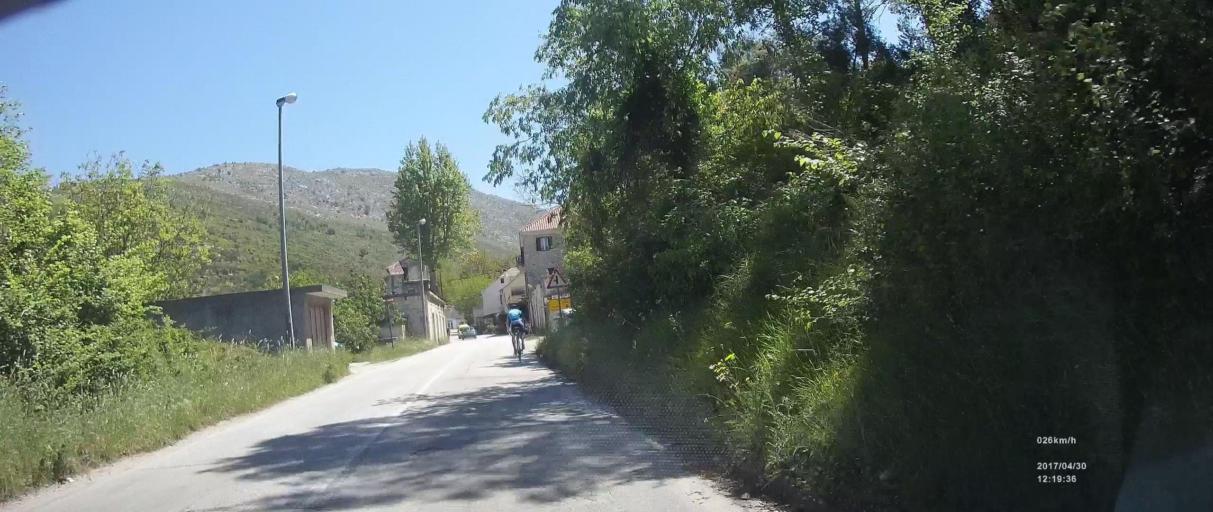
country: HR
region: Splitsko-Dalmatinska
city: Zrnovnica
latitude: 43.5164
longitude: 16.5553
